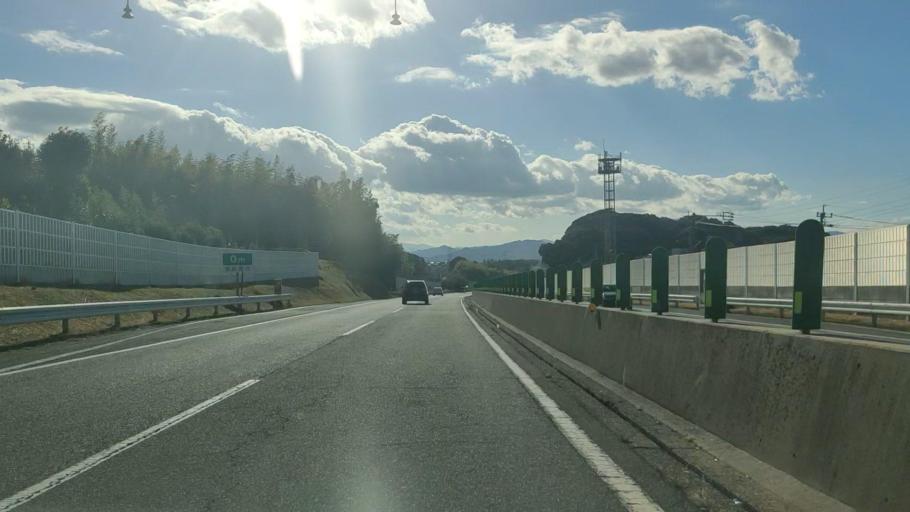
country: JP
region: Fukuoka
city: Nakama
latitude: 33.8245
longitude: 130.7625
